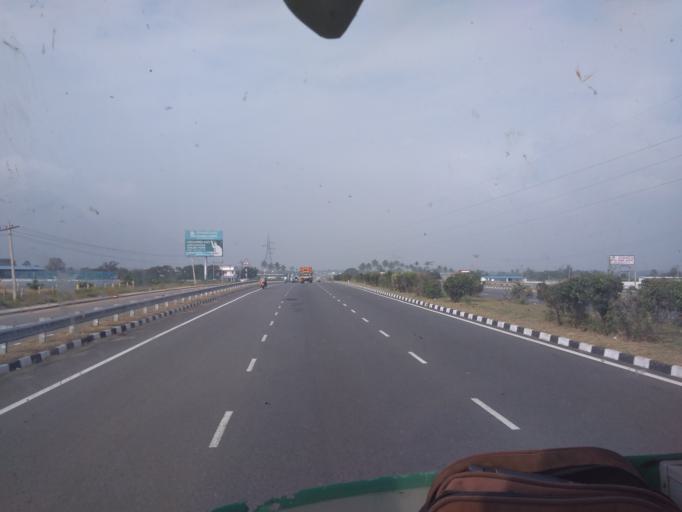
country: IN
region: Tamil Nadu
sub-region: Vellore
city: Pallikondai
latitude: 12.9105
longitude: 78.9911
